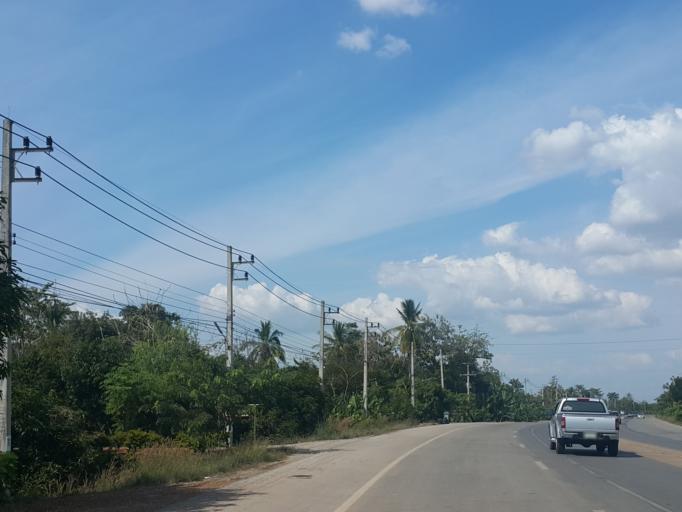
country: TH
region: Sukhothai
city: Si Samrong
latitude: 17.2325
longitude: 99.8465
